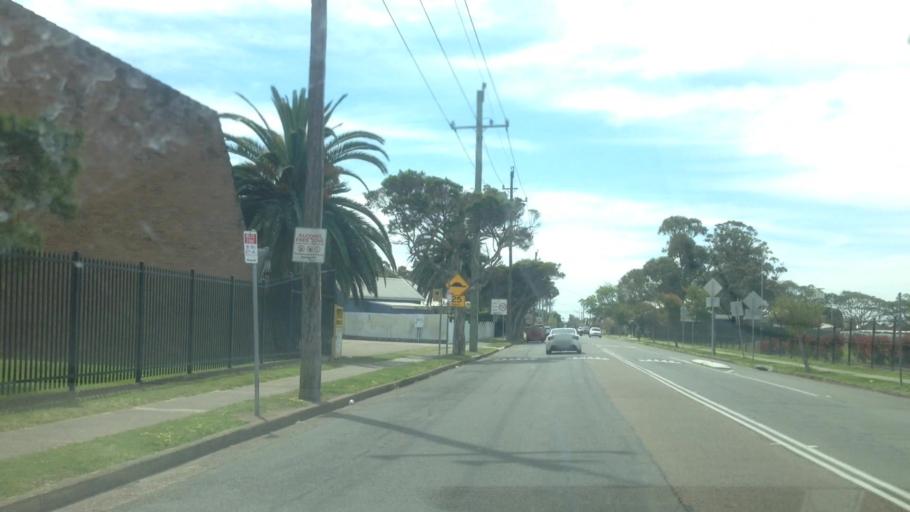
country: AU
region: New South Wales
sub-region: Newcastle
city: Broadmeadow
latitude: -32.9292
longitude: 151.7364
